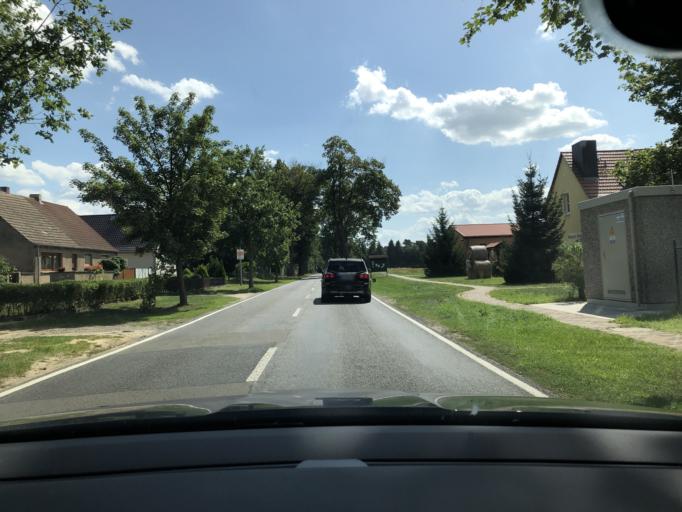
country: DE
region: Brandenburg
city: Ruthnick
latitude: 52.8804
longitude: 13.0019
